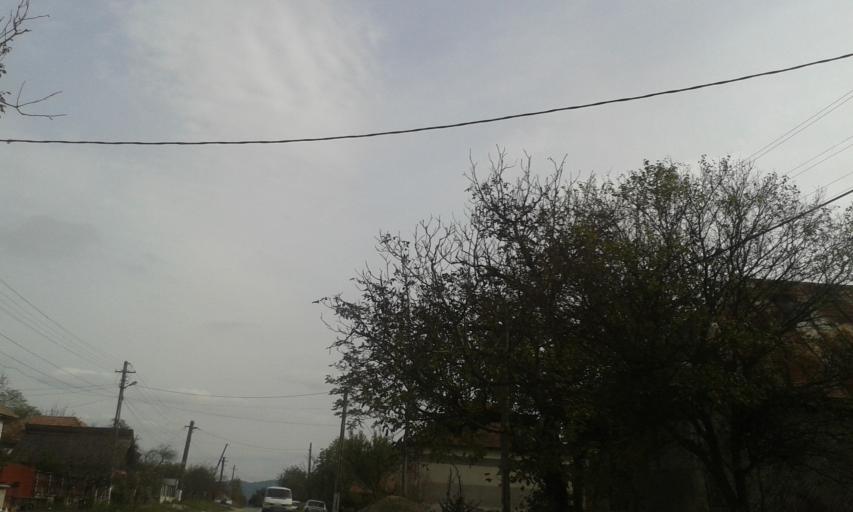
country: RO
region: Valcea
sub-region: Comuna Gradistea
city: Gradistea
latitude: 44.9025
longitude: 23.8033
